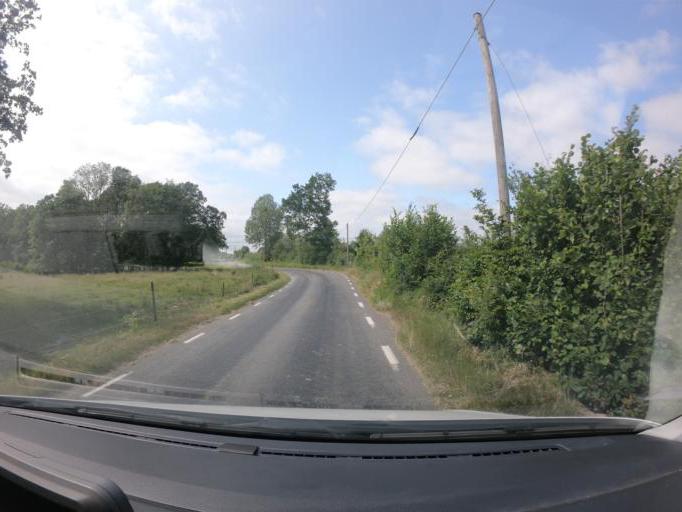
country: SE
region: Skane
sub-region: Hassleholms Kommun
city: Sosdala
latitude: 56.1208
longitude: 13.6070
